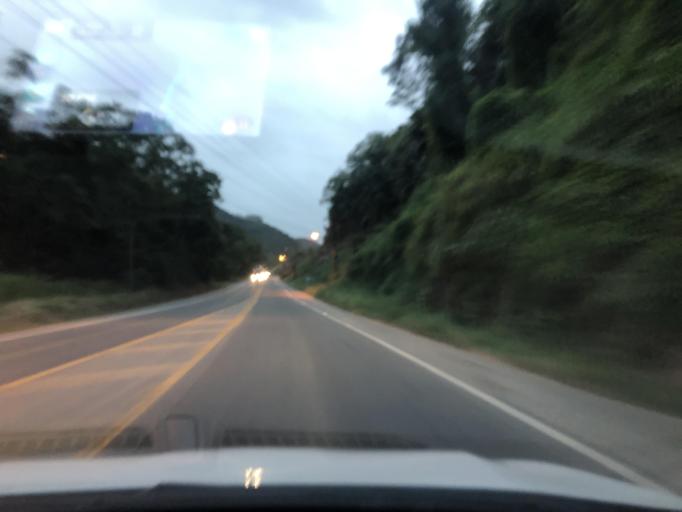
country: BR
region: Santa Catarina
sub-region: Pomerode
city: Pomerode
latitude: -26.7181
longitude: -49.0584
